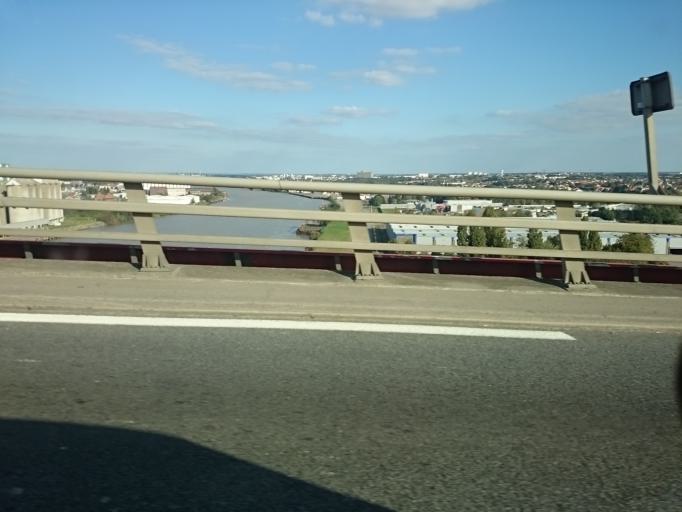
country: FR
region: Pays de la Loire
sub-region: Departement de la Loire-Atlantique
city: Bouguenais
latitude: 47.1913
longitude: -1.6135
